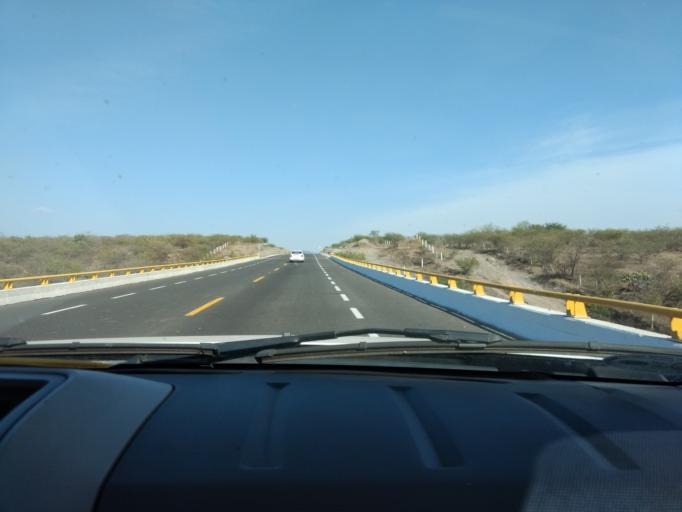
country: MX
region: Morelos
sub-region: Ayala
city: El Salitre
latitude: 18.6674
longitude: -98.9649
